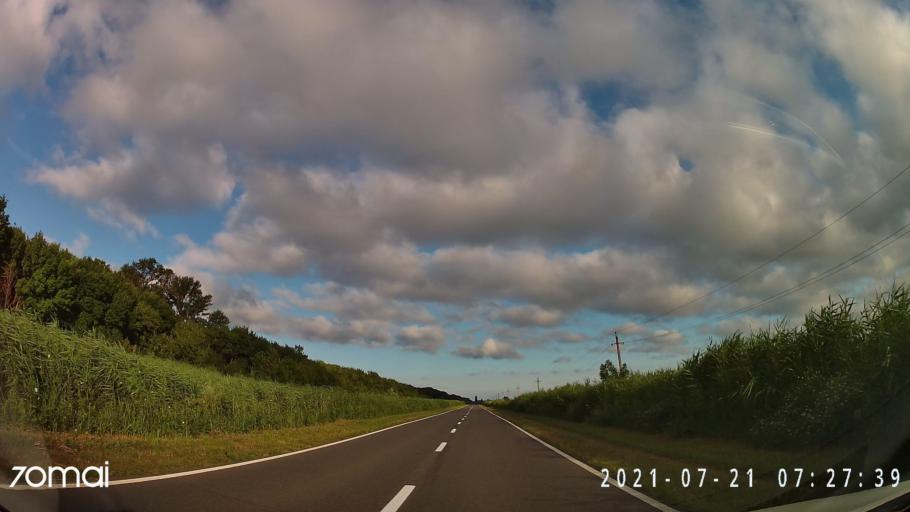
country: RO
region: Tulcea
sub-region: Oras Isaccea
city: Isaccea
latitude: 45.3052
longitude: 28.4118
